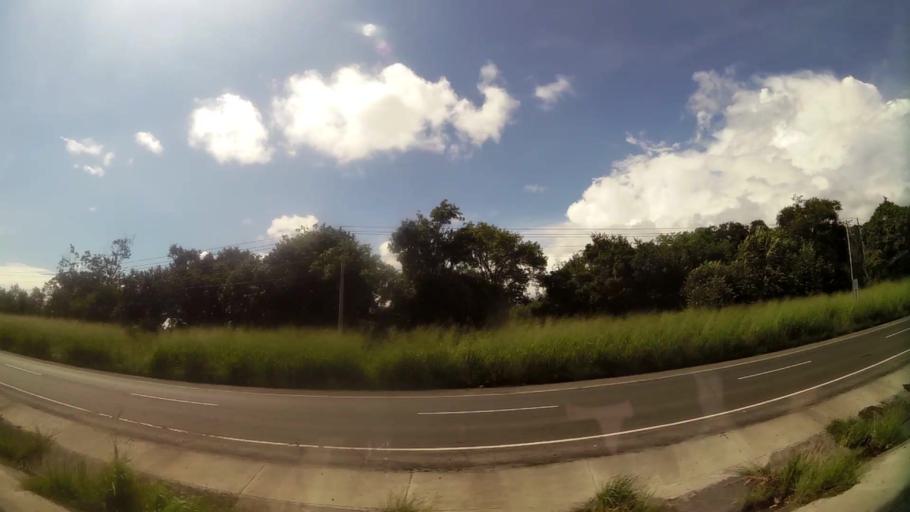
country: PA
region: Panama
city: Bejuco
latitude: 8.6159
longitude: -79.8809
